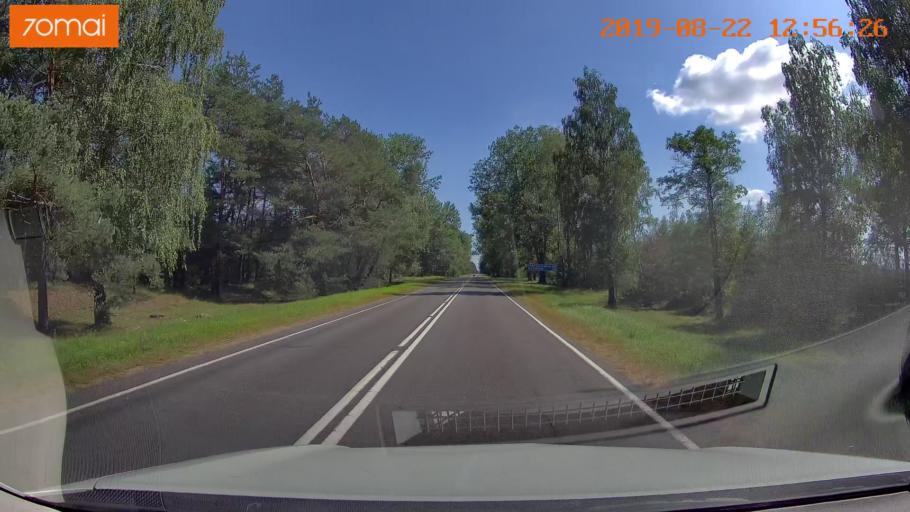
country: BY
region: Minsk
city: Prawdzinski
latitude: 53.4329
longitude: 27.7309
